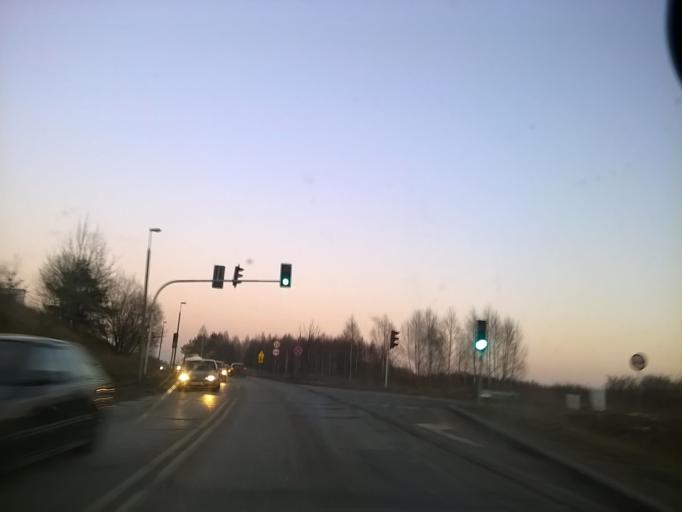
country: PL
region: Warmian-Masurian Voivodeship
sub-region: Powiat olsztynski
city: Olsztyn
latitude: 53.7804
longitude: 20.5500
